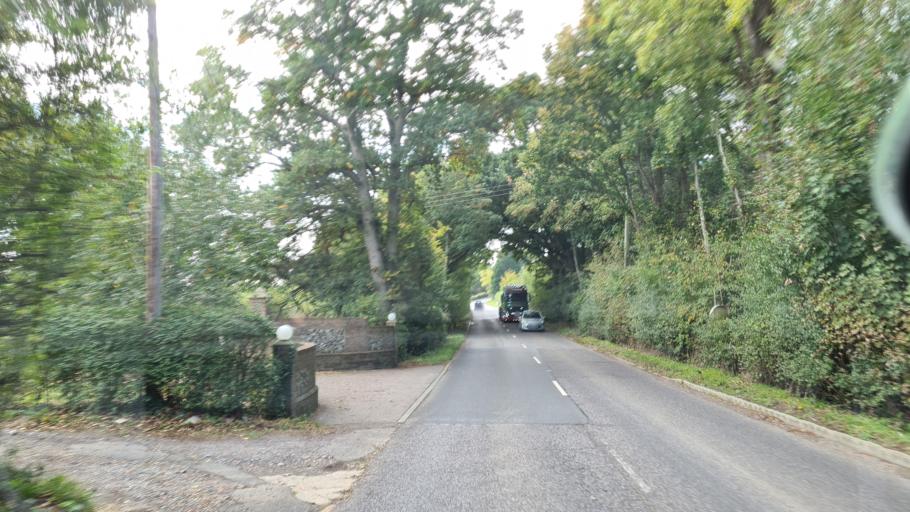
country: GB
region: England
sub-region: East Sussex
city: Hailsham
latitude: 50.8818
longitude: 0.2940
